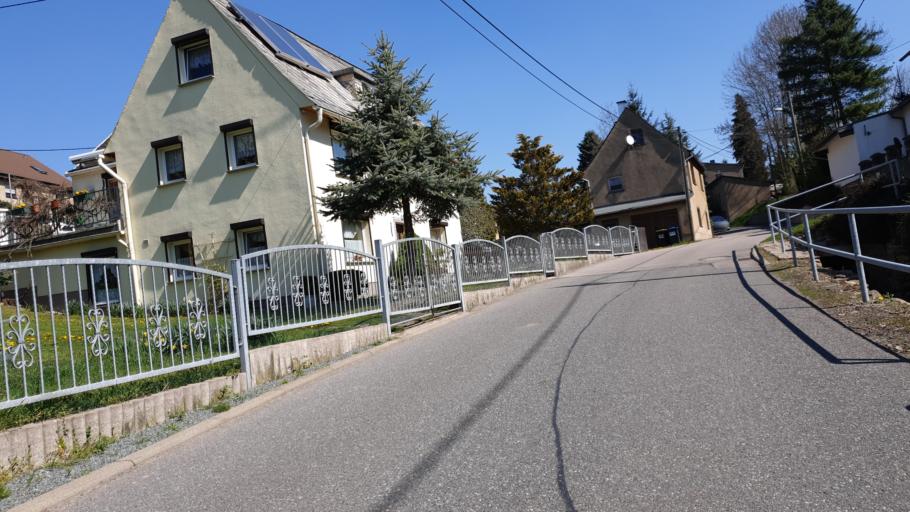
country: DE
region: Saxony
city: Taura
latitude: 50.9432
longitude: 12.8492
